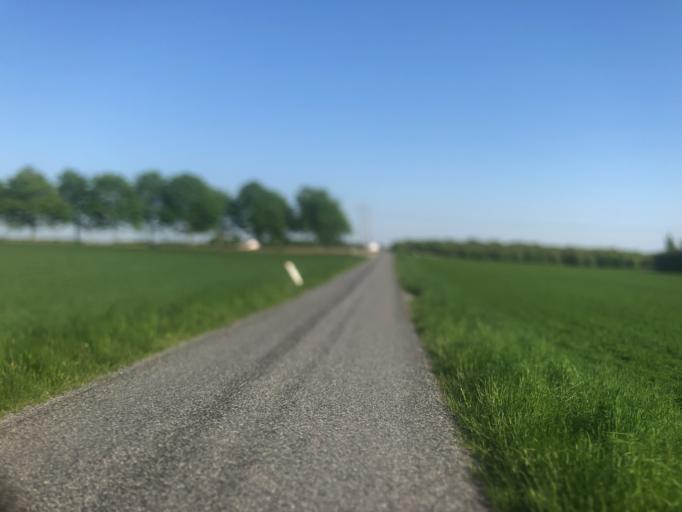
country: DK
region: Zealand
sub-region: Ringsted Kommune
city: Ringsted
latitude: 55.4759
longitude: 11.8142
